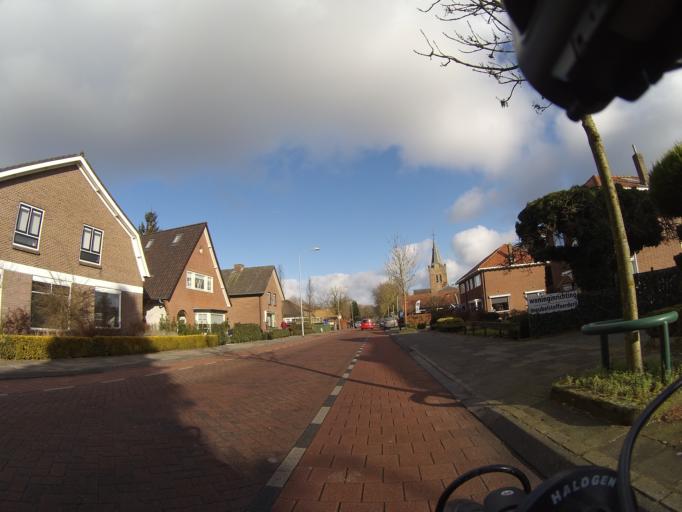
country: NL
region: Utrecht
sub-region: Gemeente Leusden
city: Leusden
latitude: 52.1742
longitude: 5.4470
